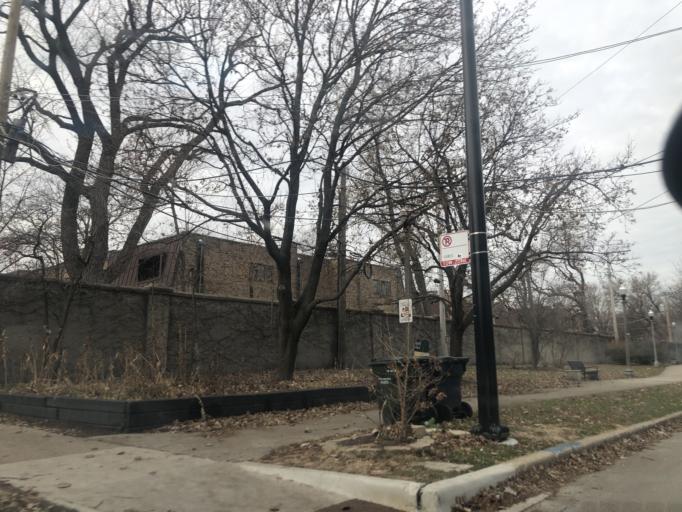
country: US
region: Illinois
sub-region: Cook County
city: Lincolnwood
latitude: 41.9512
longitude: -87.6568
